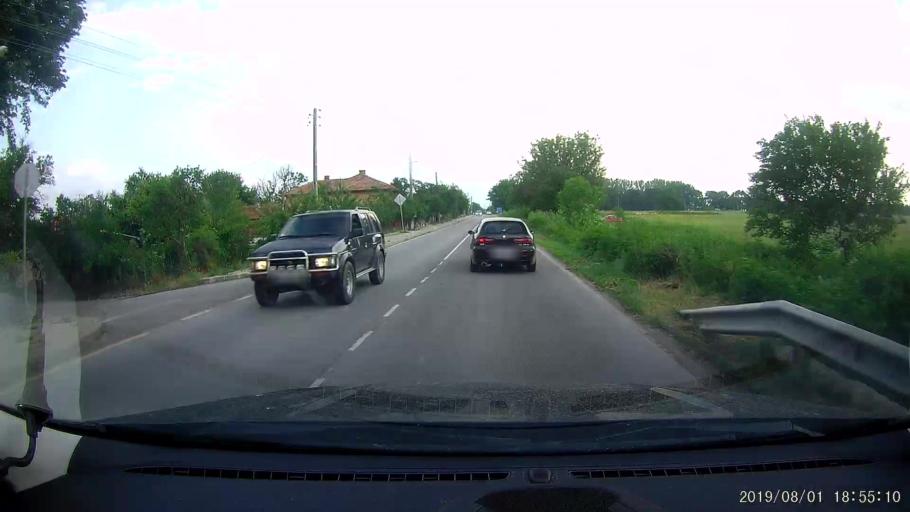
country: BG
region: Shumen
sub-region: Obshtina Shumen
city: Shumen
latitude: 43.1848
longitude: 27.0044
